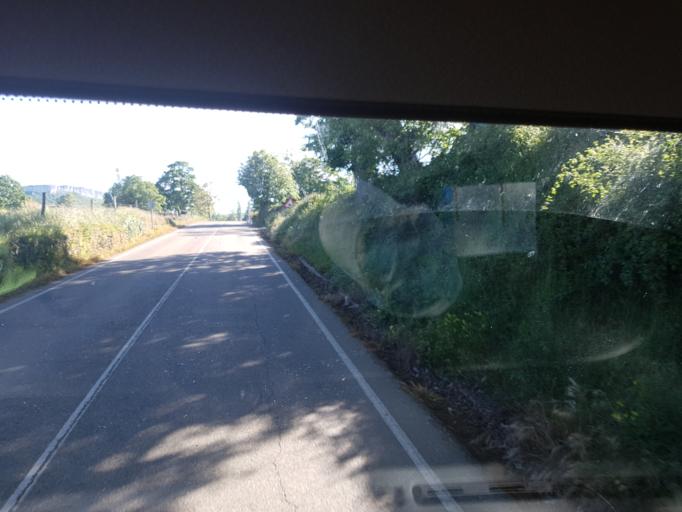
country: ES
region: Castille and Leon
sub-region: Provincia de Burgos
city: Espinosa de los Monteros
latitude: 43.0737
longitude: -3.5580
